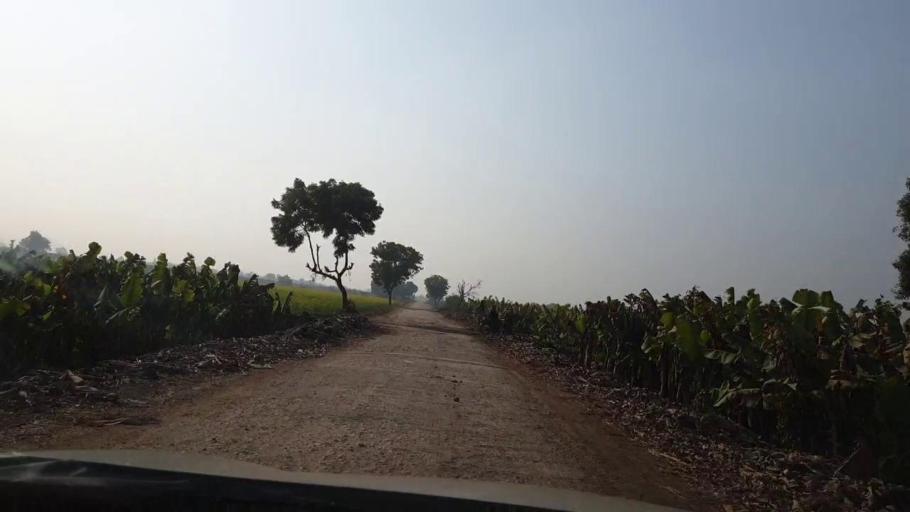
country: PK
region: Sindh
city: Matiari
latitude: 25.6841
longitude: 68.5241
